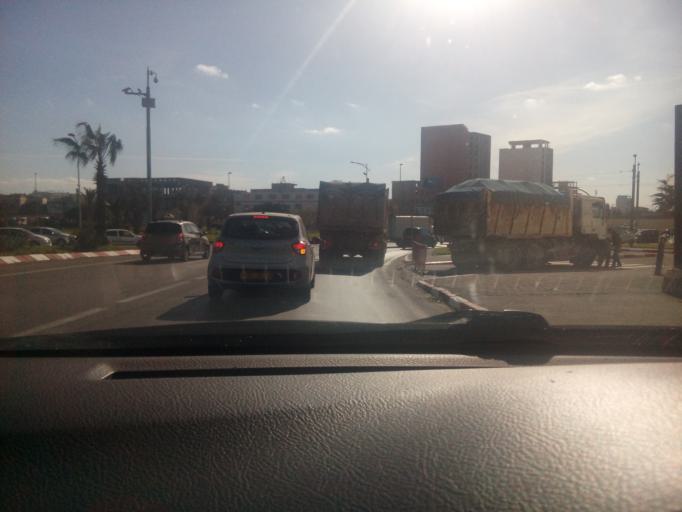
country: DZ
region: Oran
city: Oran
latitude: 35.6976
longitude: -0.6053
